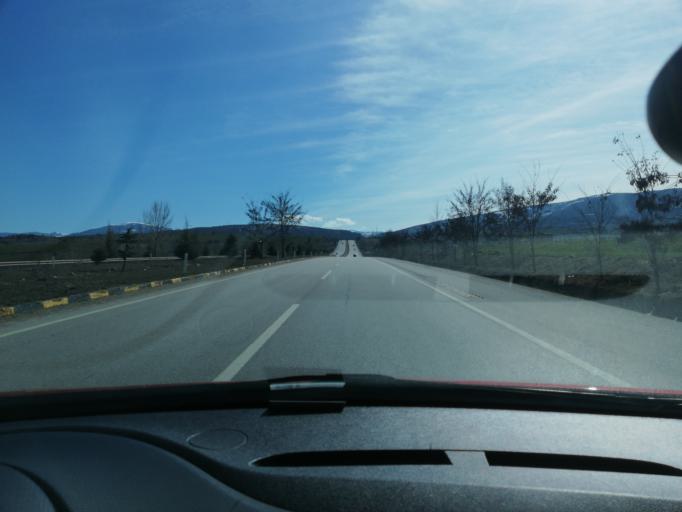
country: TR
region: Karabuk
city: Eskipazar
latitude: 40.9238
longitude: 32.5840
